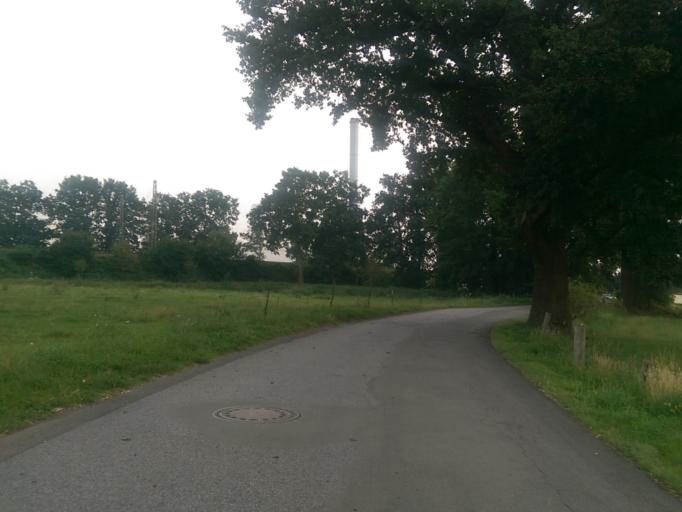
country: DE
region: North Rhine-Westphalia
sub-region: Regierungsbezirk Detmold
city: Rheda-Wiedenbruck
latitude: 51.8668
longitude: 8.3192
